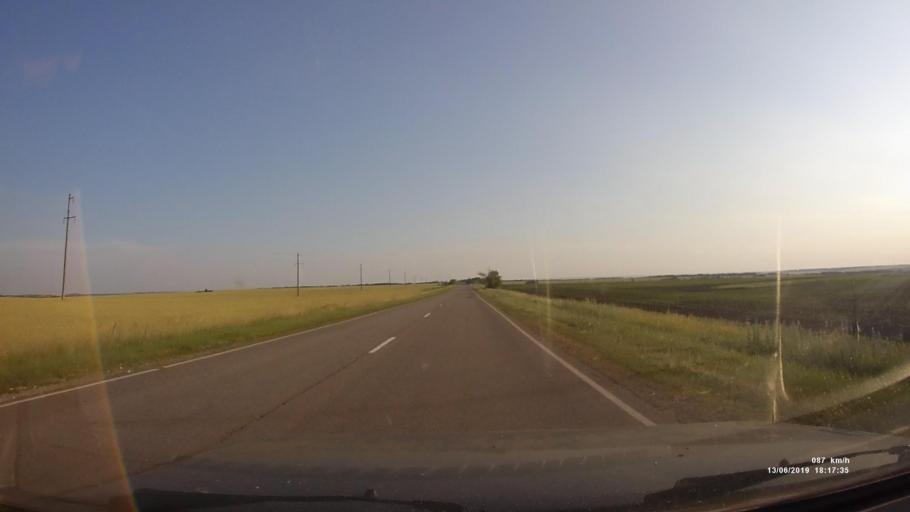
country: RU
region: Rostov
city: Kazanskaya
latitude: 49.9182
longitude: 41.3235
